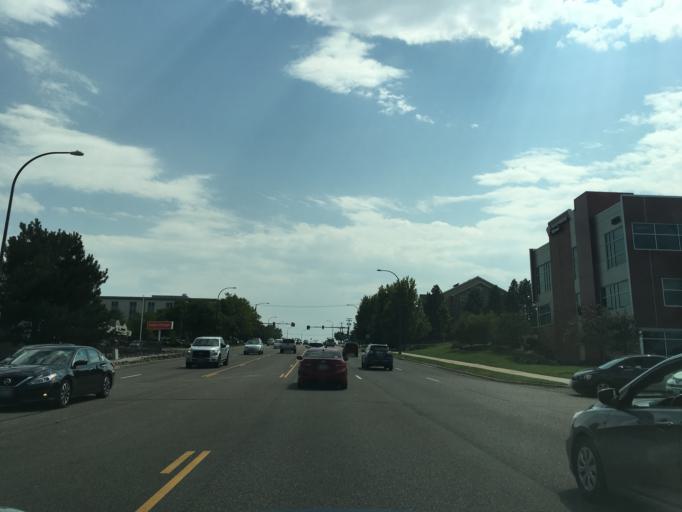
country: US
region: Colorado
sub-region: Jefferson County
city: Applewood
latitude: 39.7310
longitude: -105.1285
